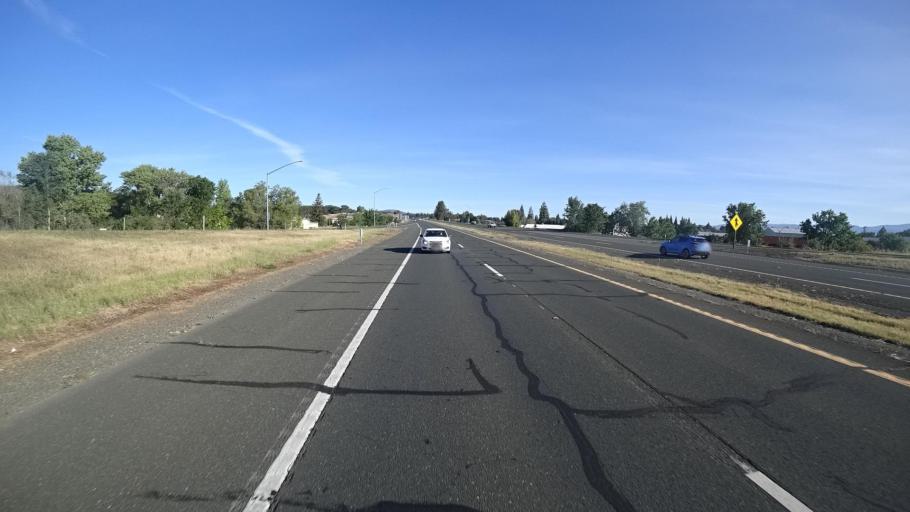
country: US
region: California
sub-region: Lake County
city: Lakeport
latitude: 39.0343
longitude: -122.9249
